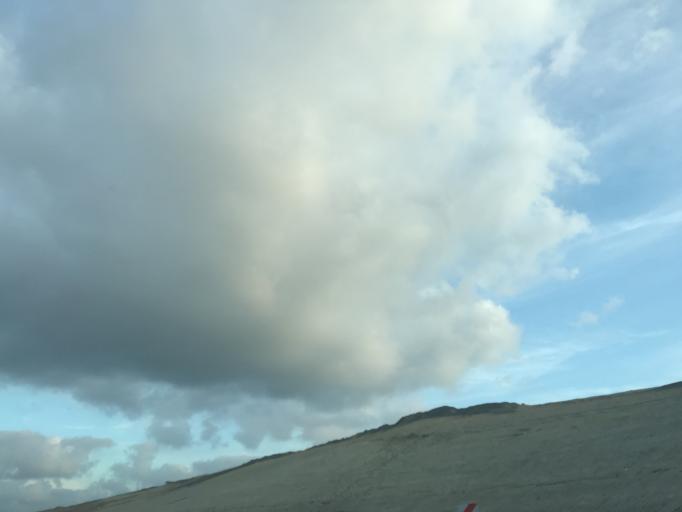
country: TR
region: Istanbul
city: Durusu
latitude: 41.2538
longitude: 28.7072
